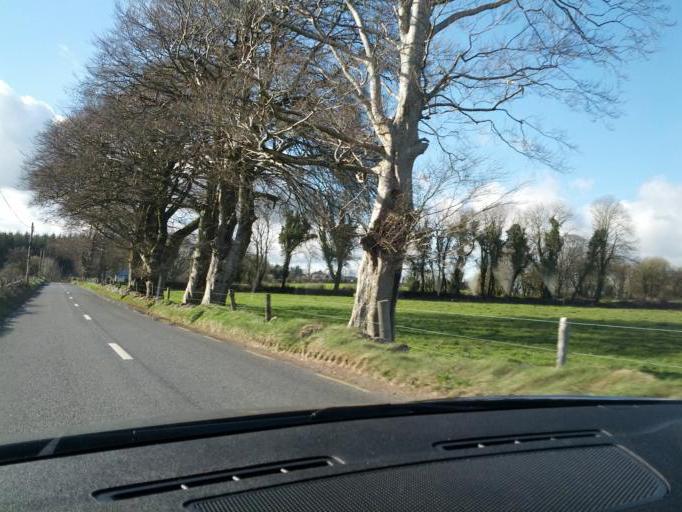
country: IE
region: Connaught
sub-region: Roscommon
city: Castlerea
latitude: 53.5467
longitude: -8.5576
